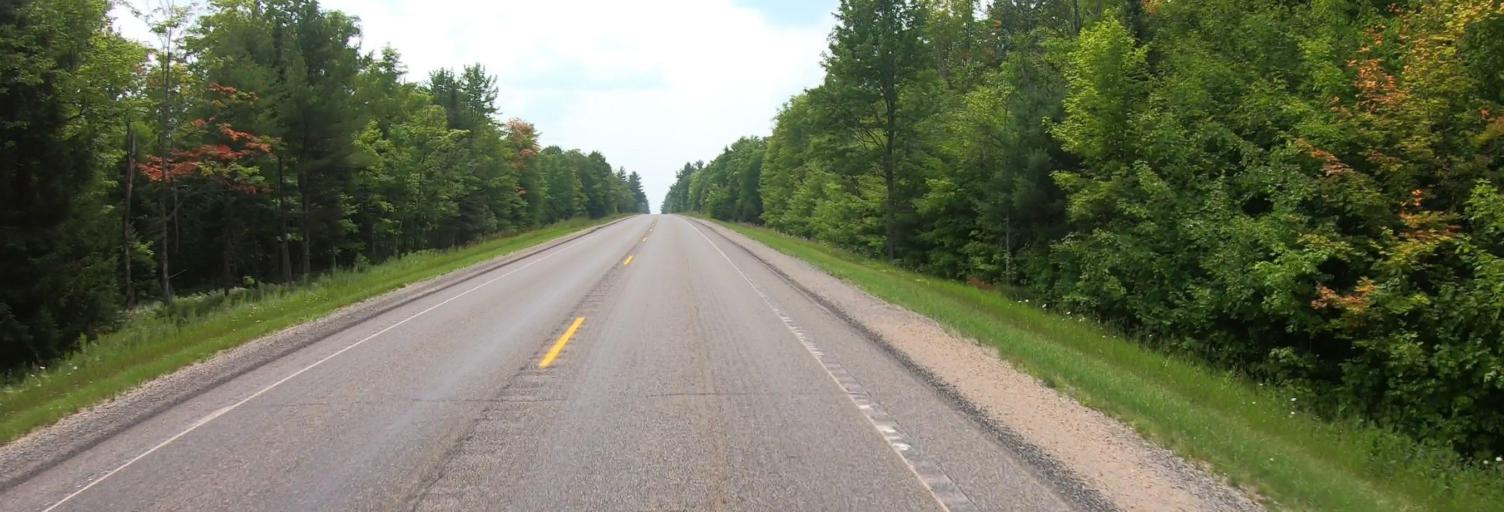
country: US
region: Michigan
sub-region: Alger County
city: Munising
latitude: 46.3541
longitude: -86.7225
